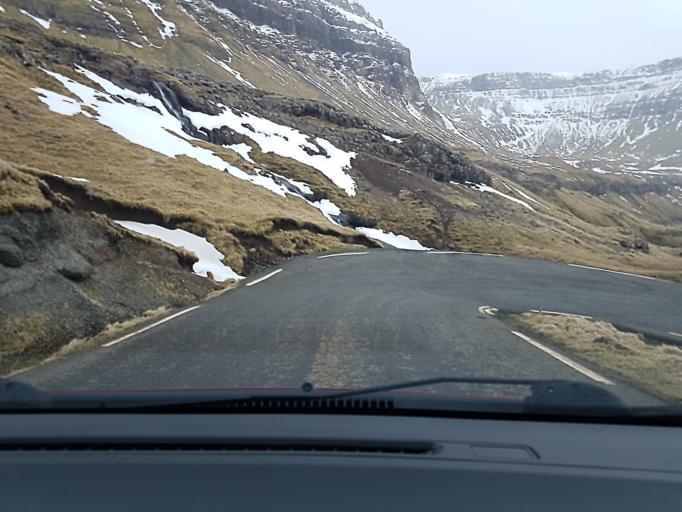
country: FO
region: Streymoy
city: Kollafjordhur
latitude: 62.0496
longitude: -6.9220
